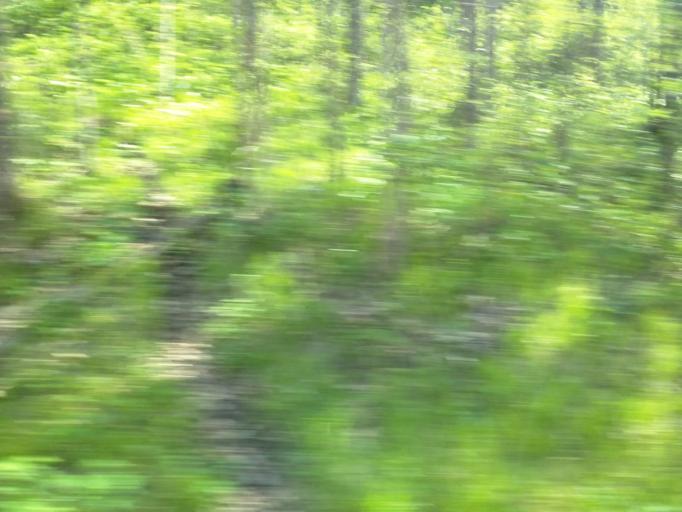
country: US
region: Wisconsin
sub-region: Monroe County
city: Cashton
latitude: 43.6339
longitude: -90.6536
